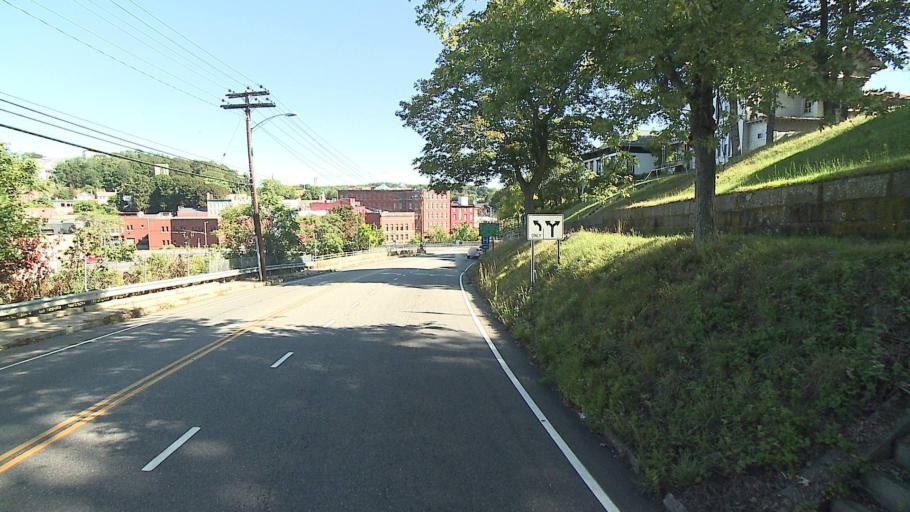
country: US
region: Connecticut
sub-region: New London County
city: Norwich
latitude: 41.5224
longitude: -72.0761
